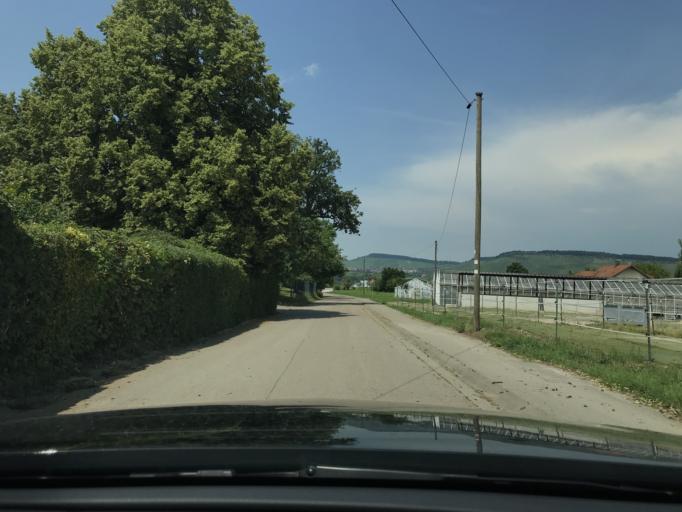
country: DE
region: Baden-Wuerttemberg
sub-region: Regierungsbezirk Stuttgart
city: Weinstadt-Endersbach
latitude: 48.8006
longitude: 9.3685
